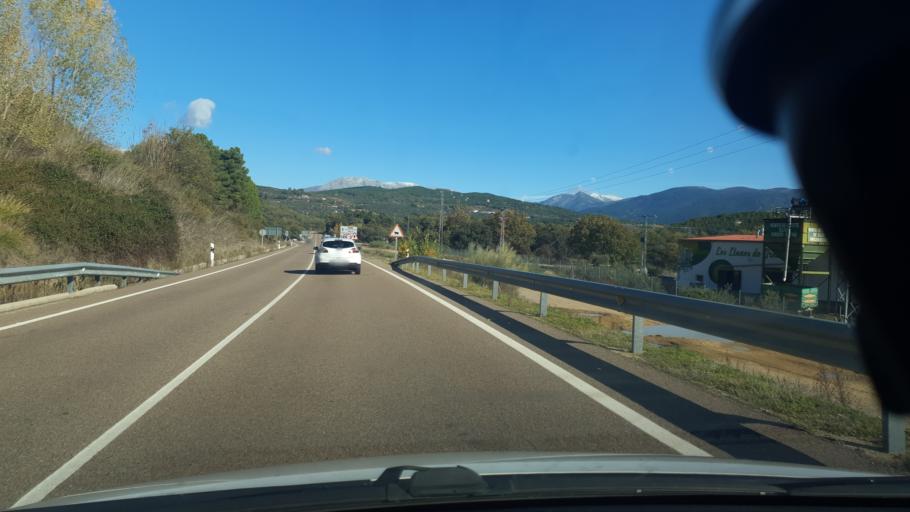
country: ES
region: Castille and Leon
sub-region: Provincia de Avila
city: Arenas de San Pedro
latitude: 40.1772
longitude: -5.0890
